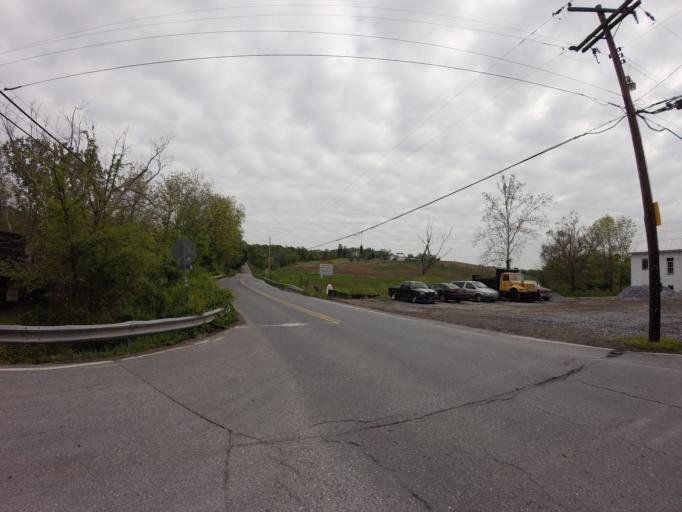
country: US
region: Maryland
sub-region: Montgomery County
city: Damascus
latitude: 39.3074
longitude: -77.2435
